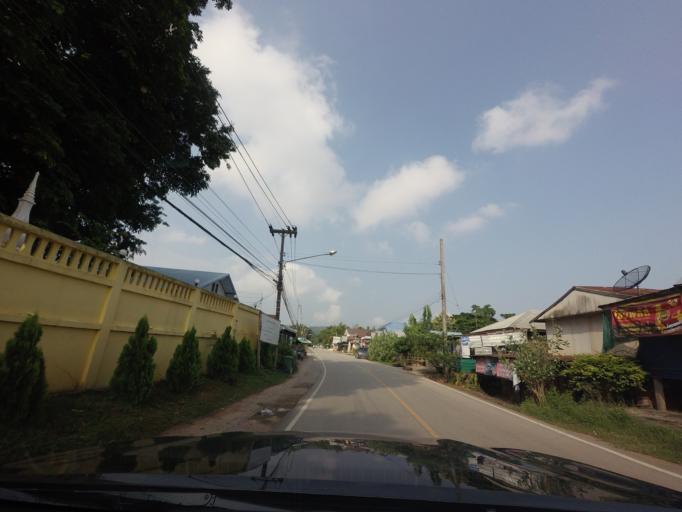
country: TH
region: Loei
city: Chiang Khan
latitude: 17.8913
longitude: 101.6461
